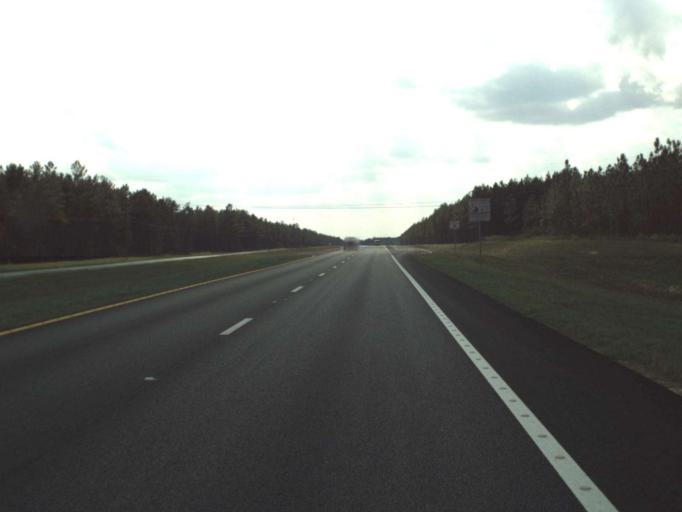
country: US
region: Florida
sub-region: Holmes County
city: Bonifay
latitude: 30.5533
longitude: -85.8210
